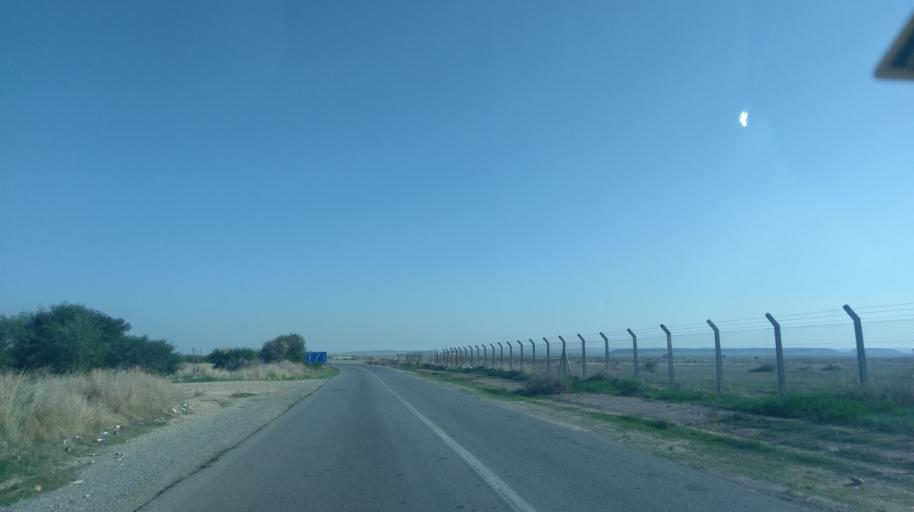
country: CY
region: Larnaka
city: Athienou
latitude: 35.1543
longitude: 33.5142
